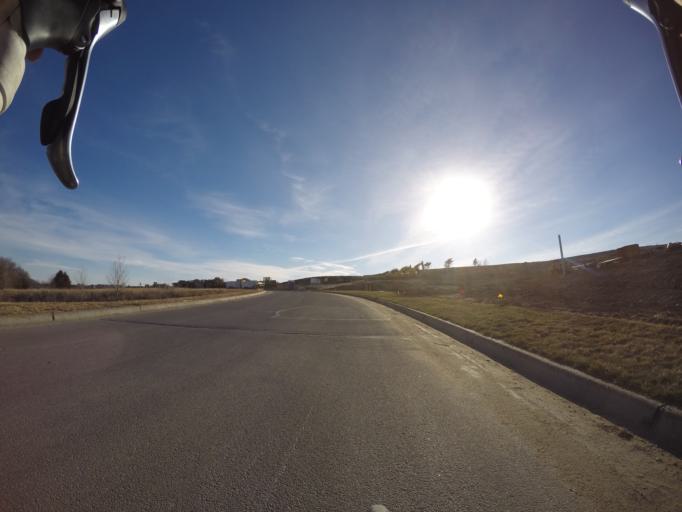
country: US
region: Kansas
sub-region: Riley County
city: Manhattan
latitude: 39.2113
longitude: -96.6355
